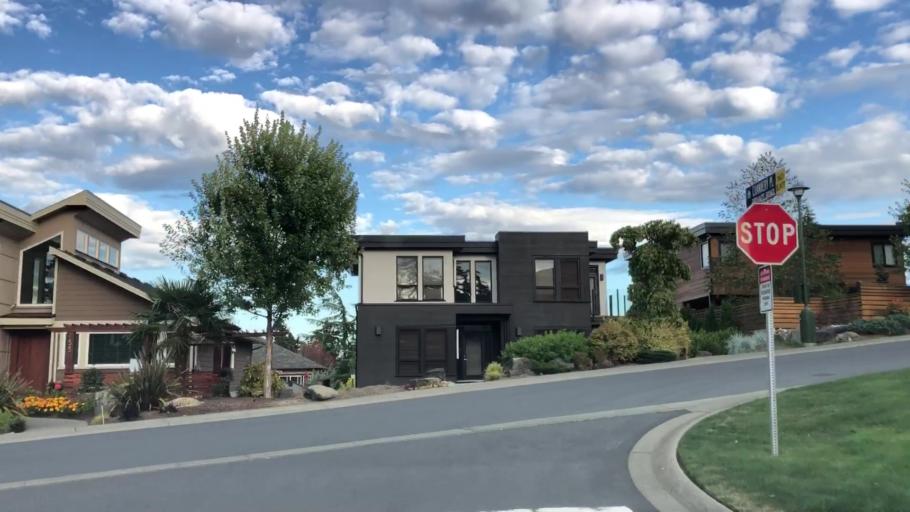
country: CA
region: British Columbia
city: Colwood
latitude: 48.4617
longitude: -123.4338
